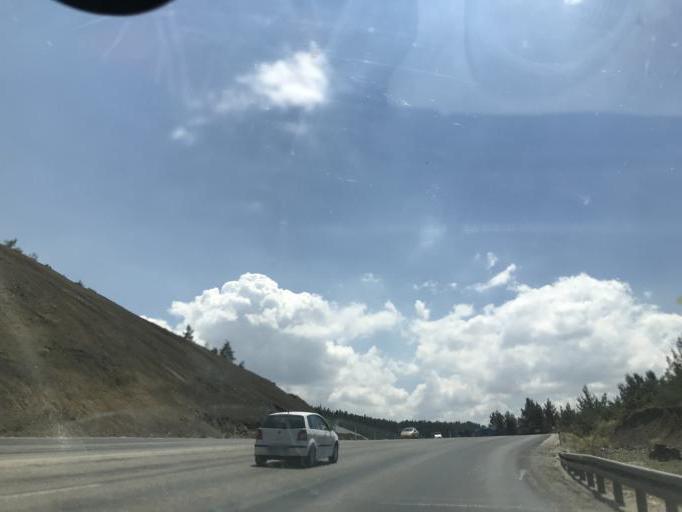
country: TR
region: Denizli
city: Serinhisar
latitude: 37.6554
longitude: 29.2282
